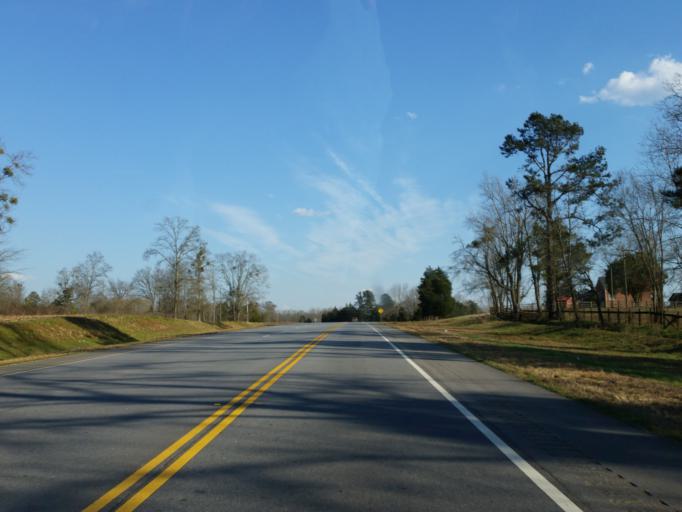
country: US
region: Georgia
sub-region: Monroe County
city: Forsyth
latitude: 33.0318
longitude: -83.9886
